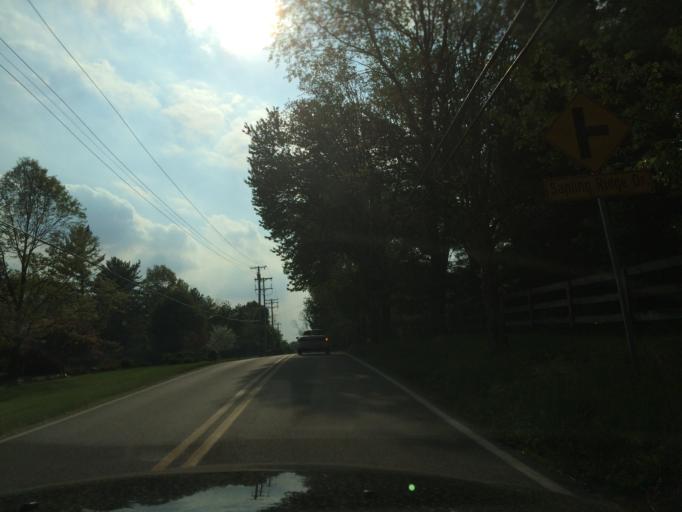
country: US
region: Maryland
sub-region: Howard County
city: Highland
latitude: 39.2291
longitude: -77.0175
